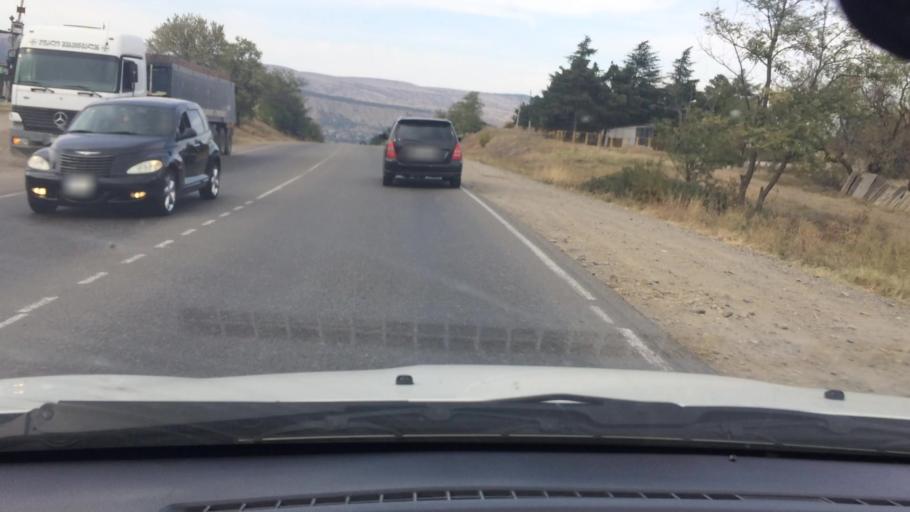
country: GE
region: T'bilisi
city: Tbilisi
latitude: 41.5913
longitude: 44.7804
